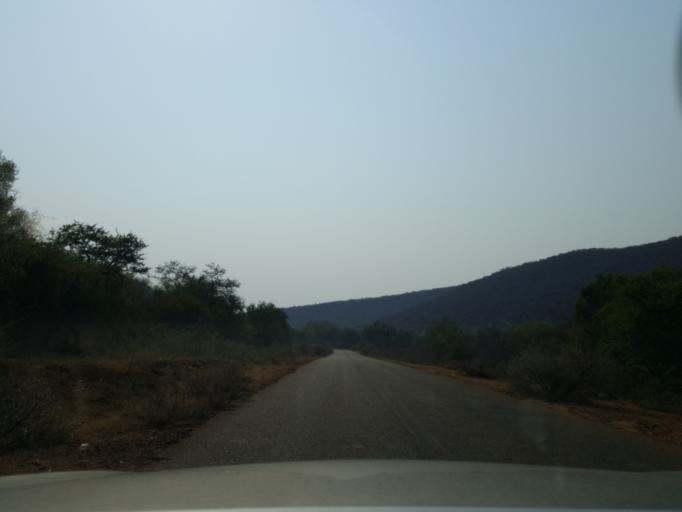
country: BW
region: South East
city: Lobatse
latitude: -25.3293
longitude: 25.7790
